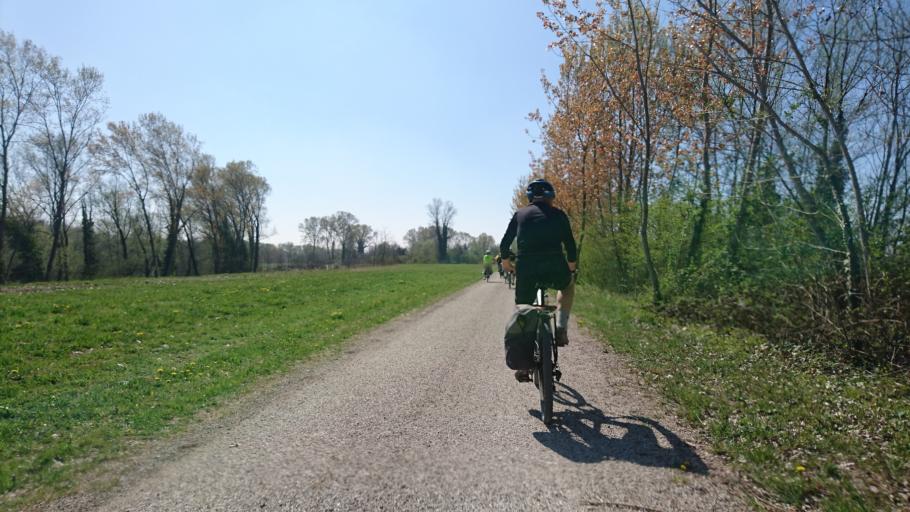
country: IT
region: Veneto
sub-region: Provincia di Padova
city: Grantorto
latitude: 45.5829
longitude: 11.7569
